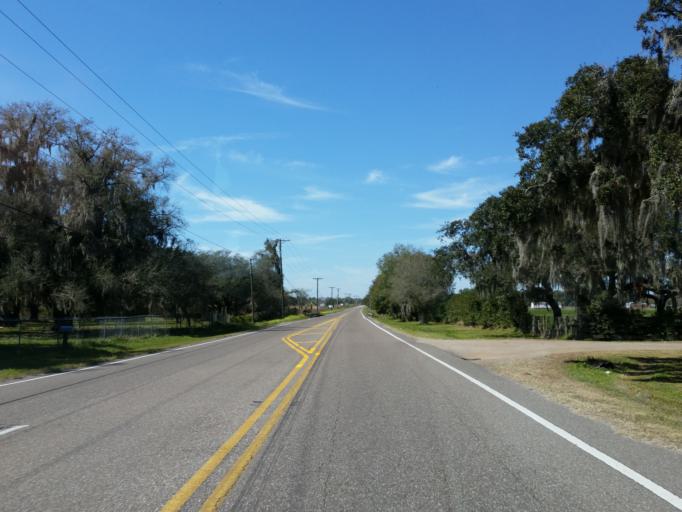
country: US
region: Florida
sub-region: Hillsborough County
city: Balm
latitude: 27.7628
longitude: -82.2323
